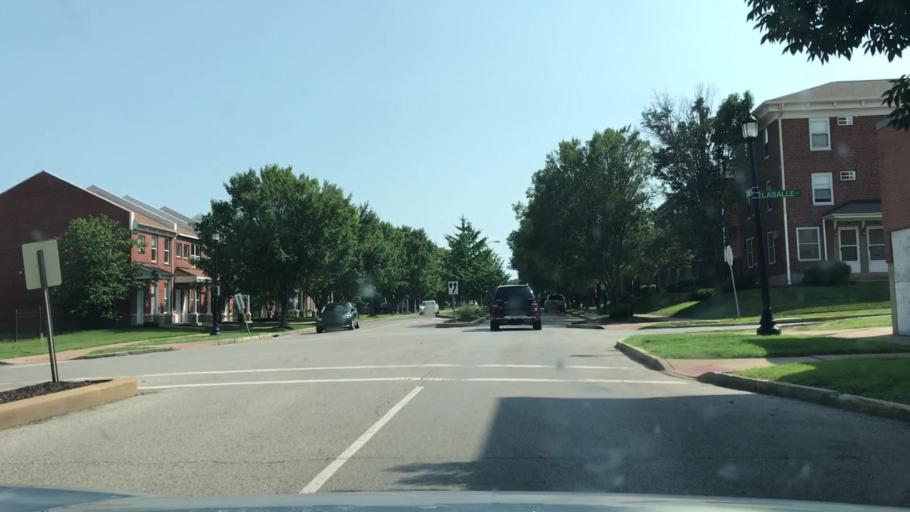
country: US
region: Missouri
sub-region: City of Saint Louis
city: St. Louis
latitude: 38.6185
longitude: -90.2049
